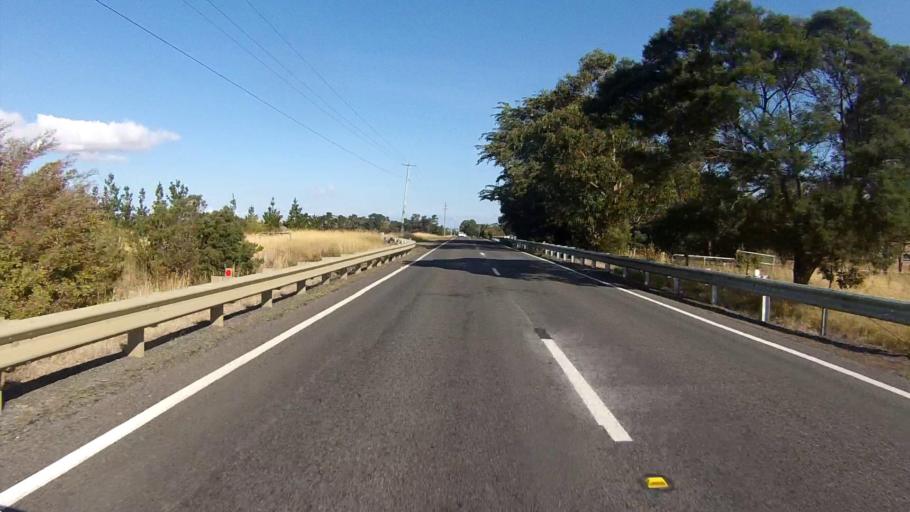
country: AU
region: Tasmania
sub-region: Sorell
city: Sorell
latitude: -42.7239
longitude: 147.5215
